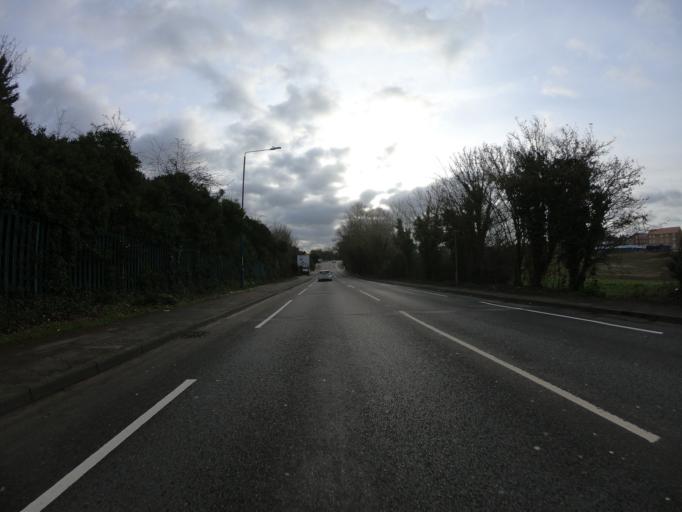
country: GB
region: England
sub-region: Kent
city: Gravesend
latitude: 51.4214
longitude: 0.3613
